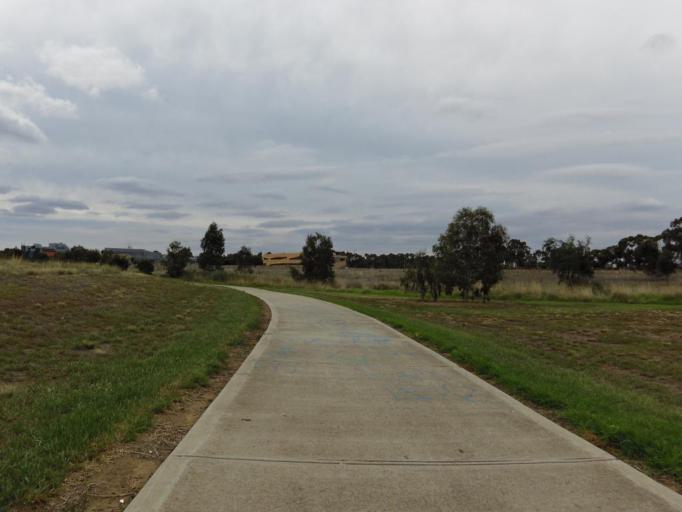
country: AU
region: Victoria
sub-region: Brimbank
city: Cairnlea
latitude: -37.7570
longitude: 144.7974
